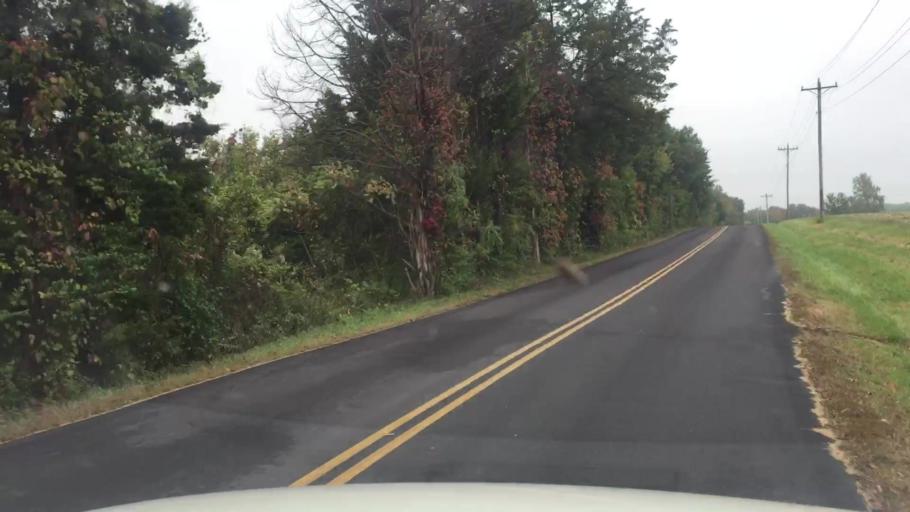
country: US
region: Missouri
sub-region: Boone County
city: Ashland
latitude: 38.8153
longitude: -92.2928
